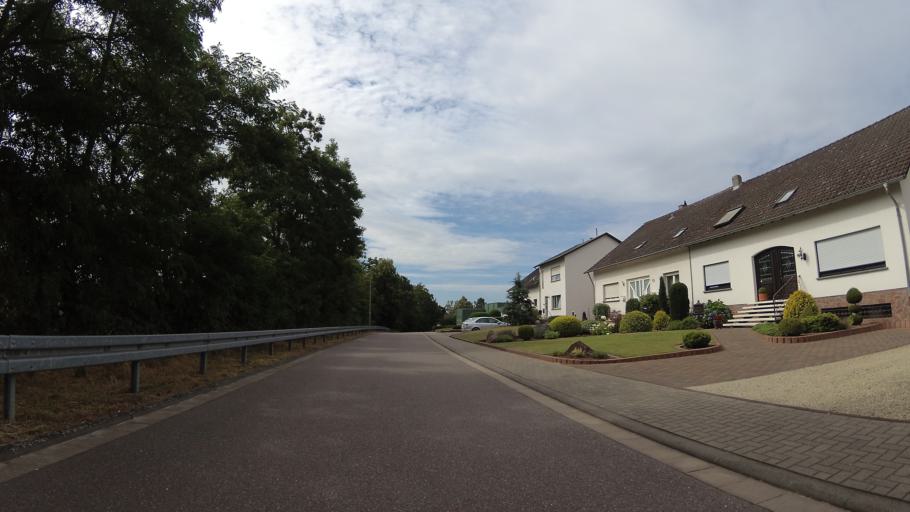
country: DE
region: Saarland
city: Schwalbach
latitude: 49.3226
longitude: 6.8169
